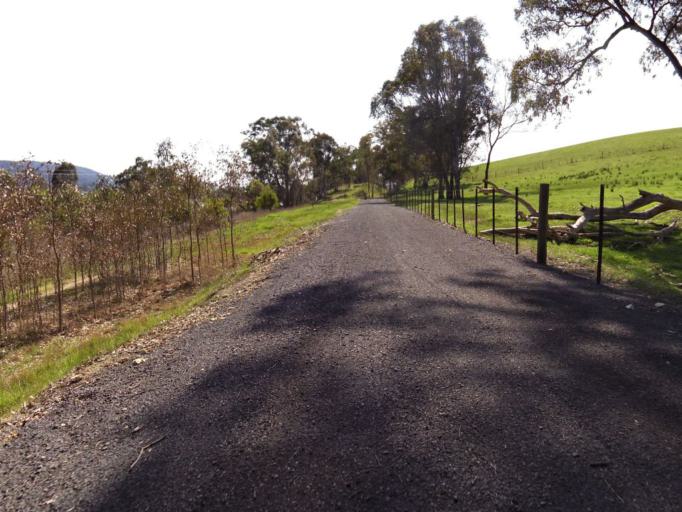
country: AU
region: Victoria
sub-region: Murrindindi
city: Alexandra
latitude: -37.1332
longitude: 145.5930
